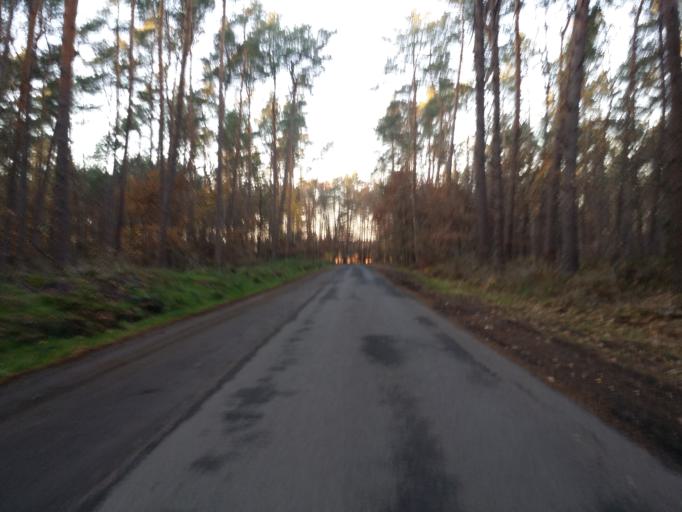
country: DE
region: Lower Saxony
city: Ahausen
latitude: 53.0823
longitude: 9.3039
